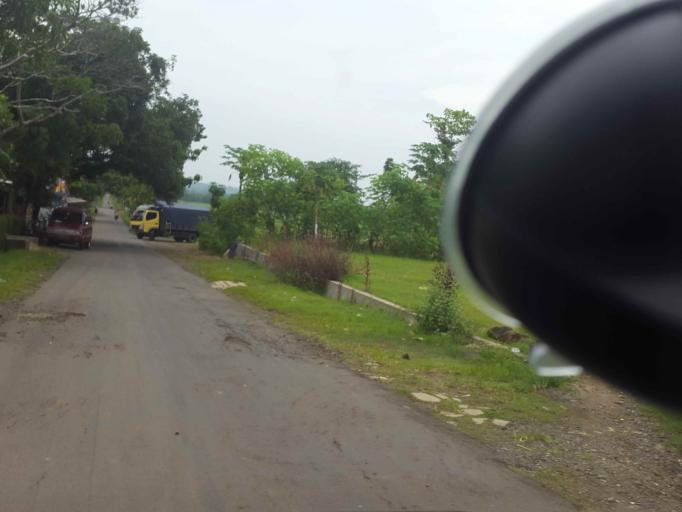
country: ID
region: Central Java
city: Banyumas
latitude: -7.5292
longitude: 109.2750
